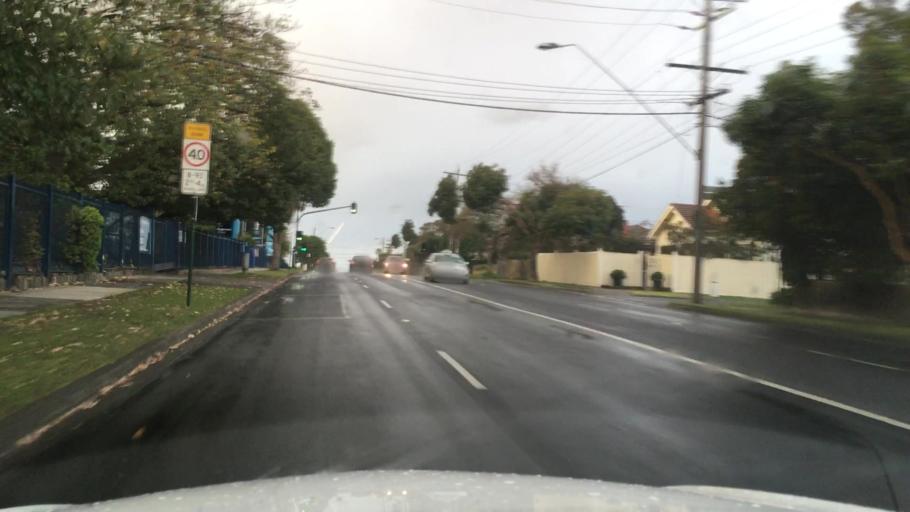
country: AU
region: Victoria
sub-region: Whitehorse
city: Box Hill South
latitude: -37.8333
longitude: 145.1210
